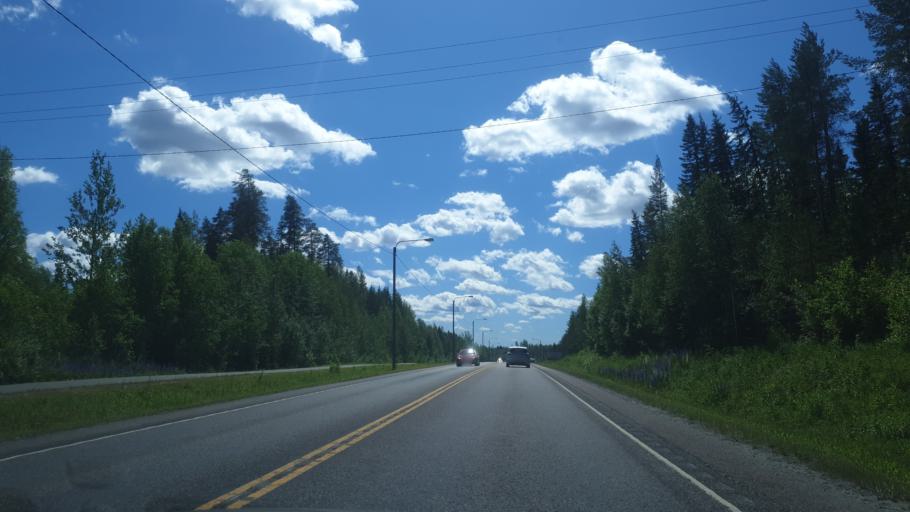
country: FI
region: Northern Savo
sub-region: Varkaus
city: Varkaus
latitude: 62.3439
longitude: 27.8207
